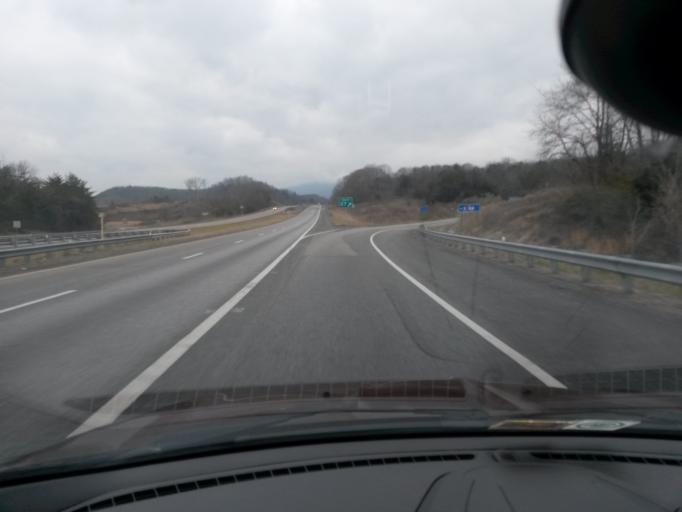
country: US
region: Virginia
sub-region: Alleghany County
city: Clifton Forge
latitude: 37.8269
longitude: -79.7896
